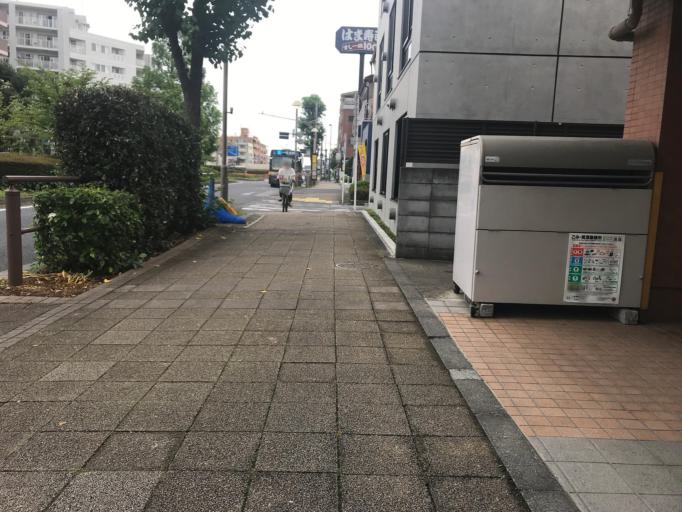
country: JP
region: Tokyo
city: Musashino
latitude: 35.7291
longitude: 139.6147
